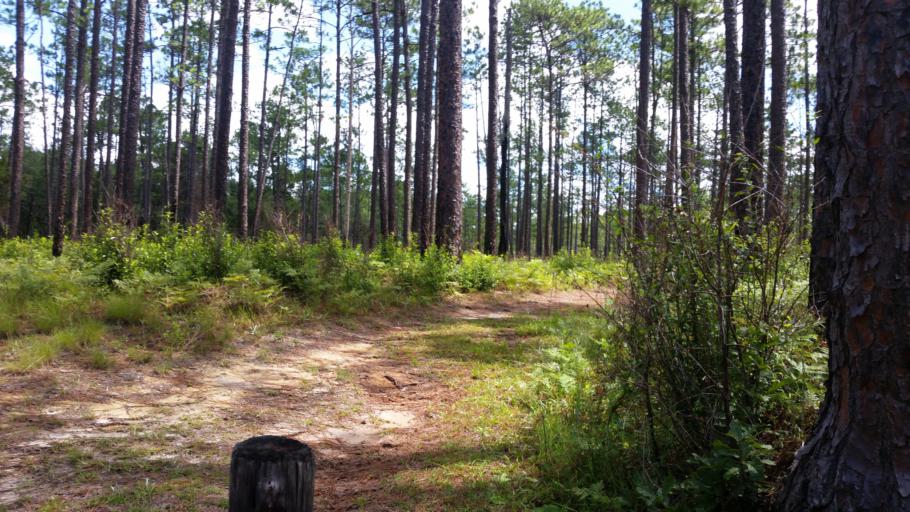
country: US
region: Florida
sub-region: Santa Rosa County
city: East Milton
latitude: 30.7034
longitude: -86.8793
